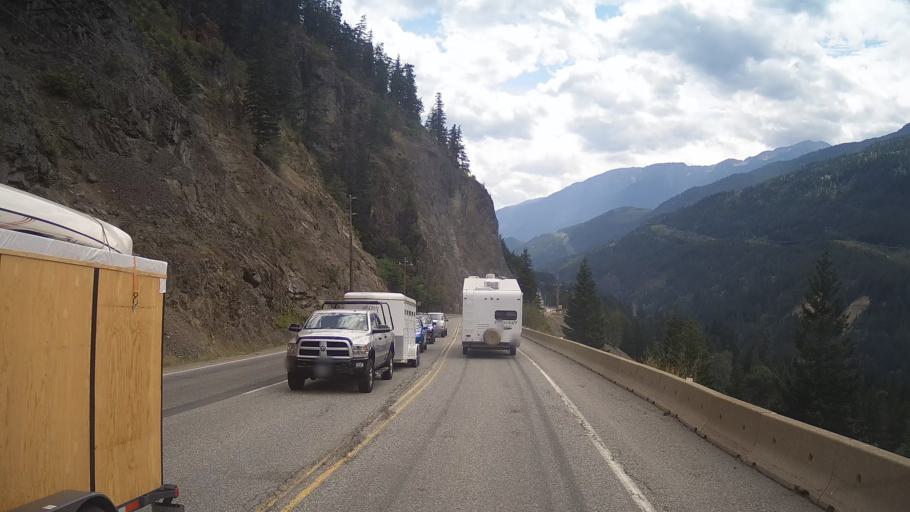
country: CA
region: British Columbia
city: Hope
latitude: 50.0680
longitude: -121.5455
